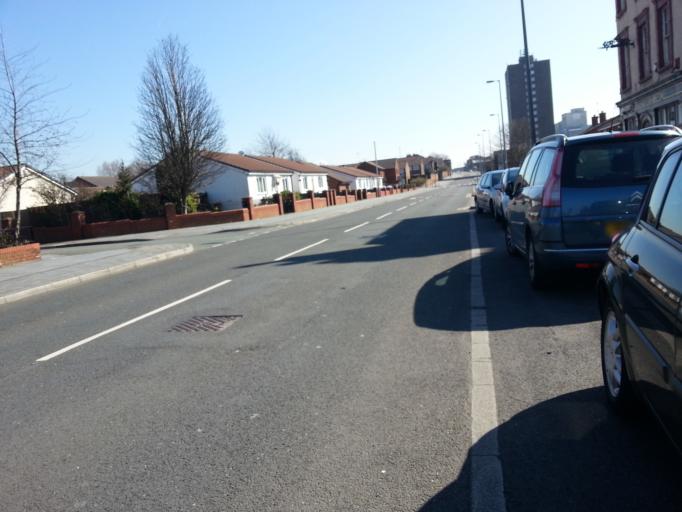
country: GB
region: England
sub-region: Liverpool
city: Liverpool
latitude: 53.3898
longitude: -2.9733
